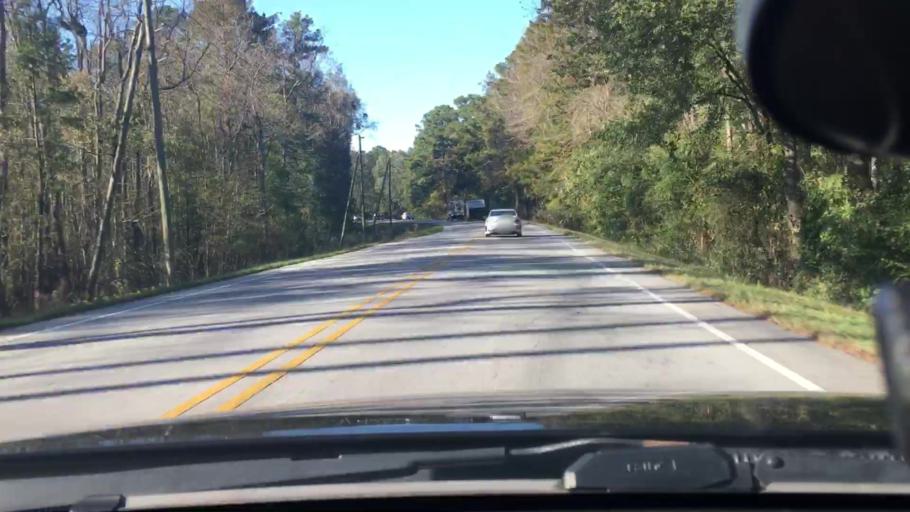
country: US
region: North Carolina
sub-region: Craven County
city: Vanceboro
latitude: 35.2334
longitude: -77.0728
